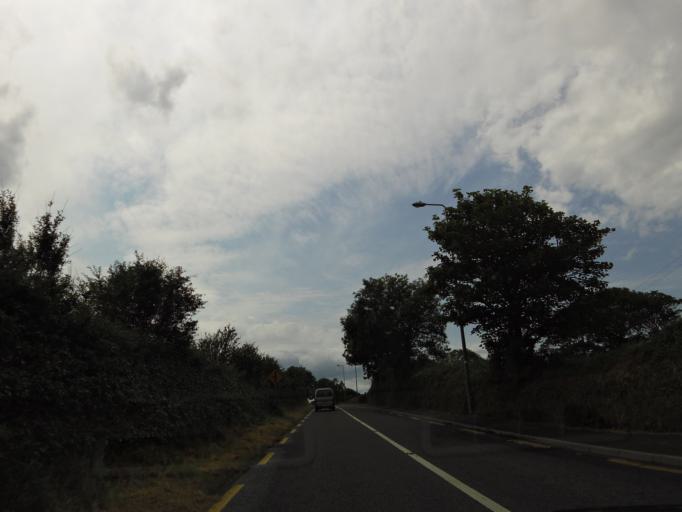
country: IE
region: Munster
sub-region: An Clar
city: Kilrush
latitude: 52.6457
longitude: -9.4700
